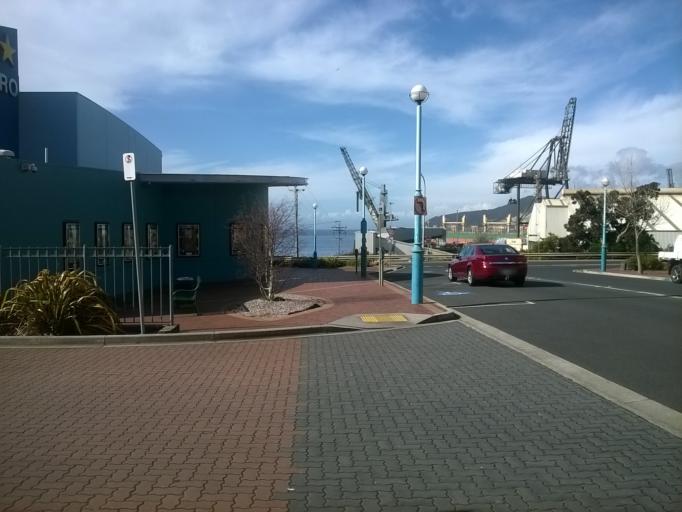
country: AU
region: Tasmania
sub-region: Burnie
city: Burnie
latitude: -41.0511
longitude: 145.9082
